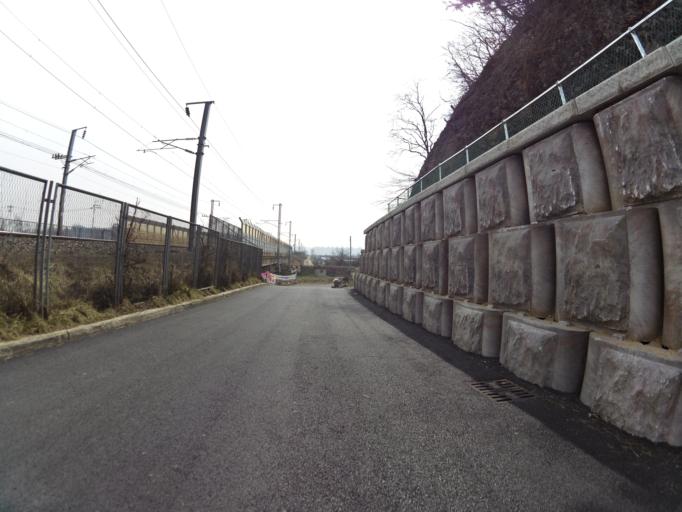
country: KR
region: Gyeongsangbuk-do
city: Gyeongsan-si
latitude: 35.8506
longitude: 128.7071
